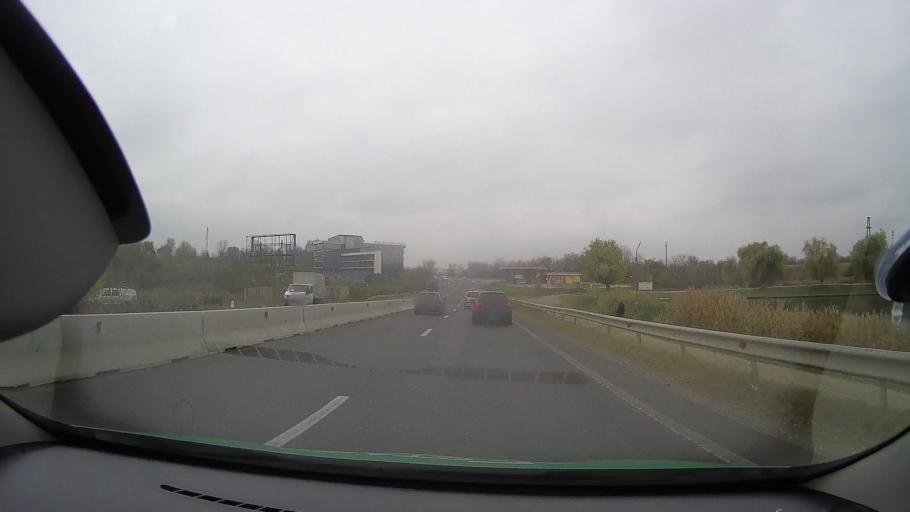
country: RO
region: Ilfov
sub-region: Comuna Ciolpani
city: Ciolpani
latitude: 44.6740
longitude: 26.0744
